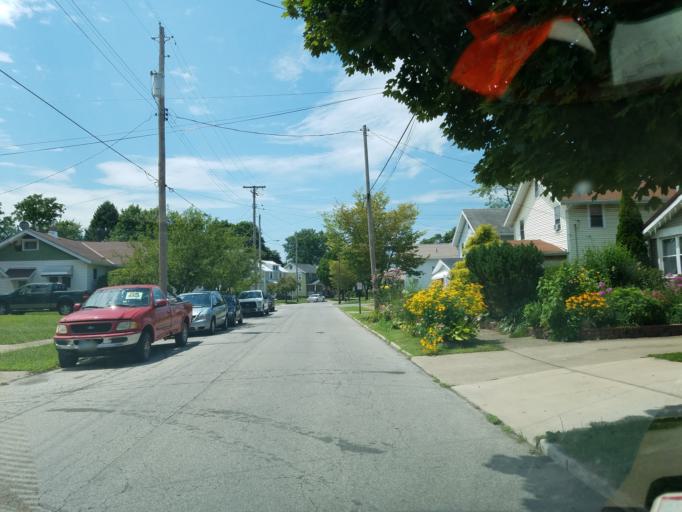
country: US
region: Ohio
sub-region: Ashland County
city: Ashland
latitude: 40.8750
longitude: -82.3247
